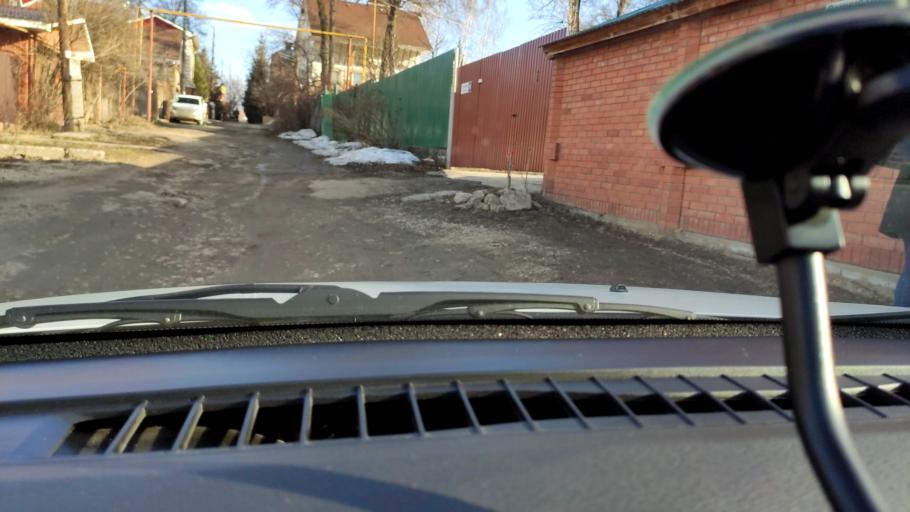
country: RU
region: Samara
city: Samara
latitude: 53.2750
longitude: 50.1989
